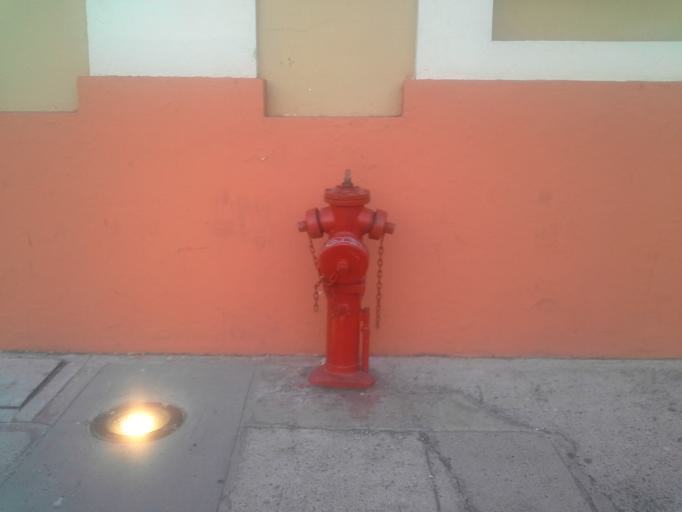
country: CO
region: Bolivar
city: Cartagena
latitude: 10.4289
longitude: -75.5482
